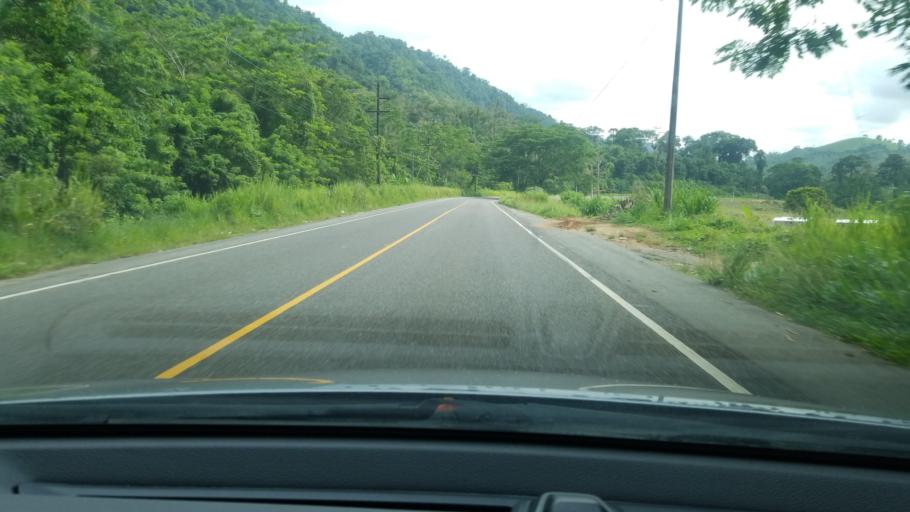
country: HN
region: Cortes
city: Potrerillos
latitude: 15.5977
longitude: -88.2993
